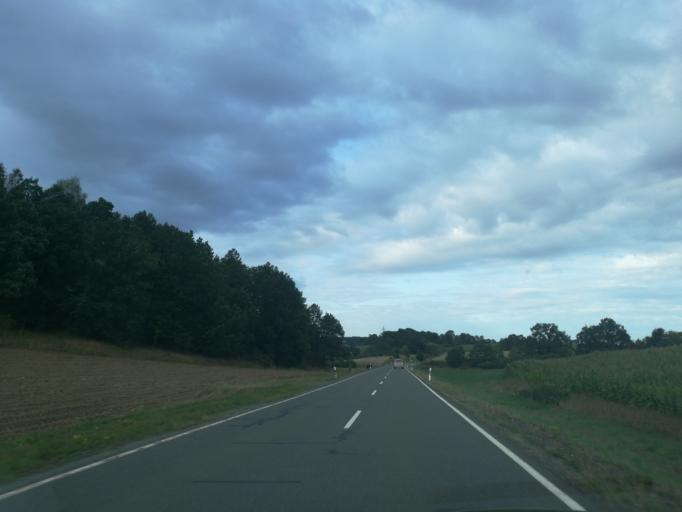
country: DE
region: Bavaria
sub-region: Upper Franconia
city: Gattendorf
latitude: 50.2995
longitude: 12.0126
